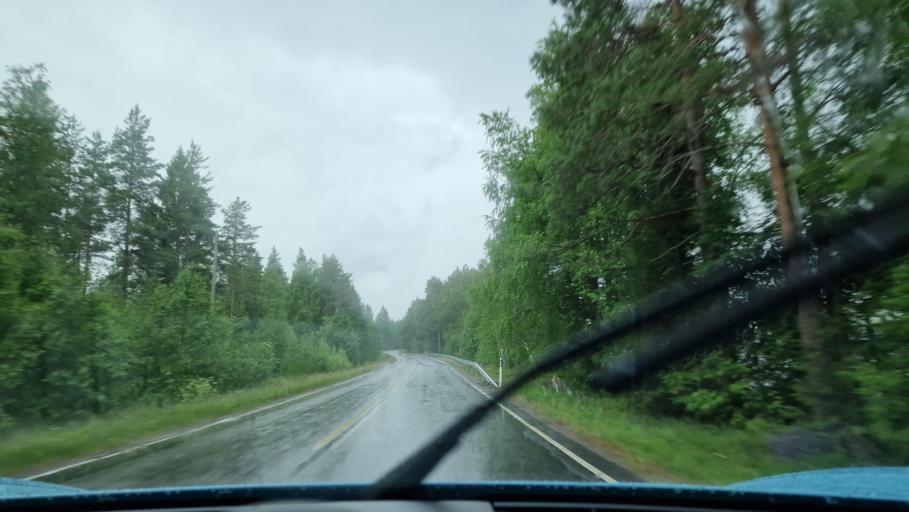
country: FI
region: Southern Ostrobothnia
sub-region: Jaerviseutu
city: Soini
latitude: 62.8219
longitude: 24.3466
